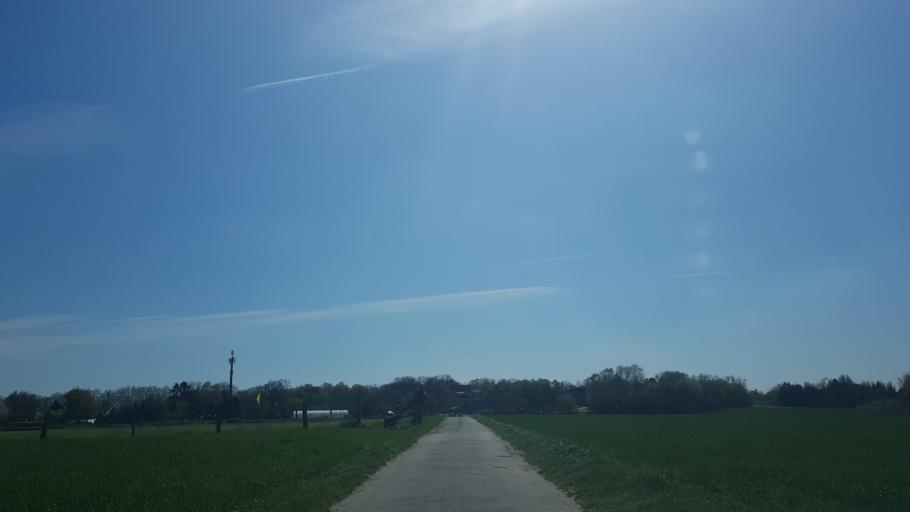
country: DE
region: North Rhine-Westphalia
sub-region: Regierungsbezirk Dusseldorf
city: Muelheim (Ruhr)
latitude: 51.4189
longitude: 6.9188
